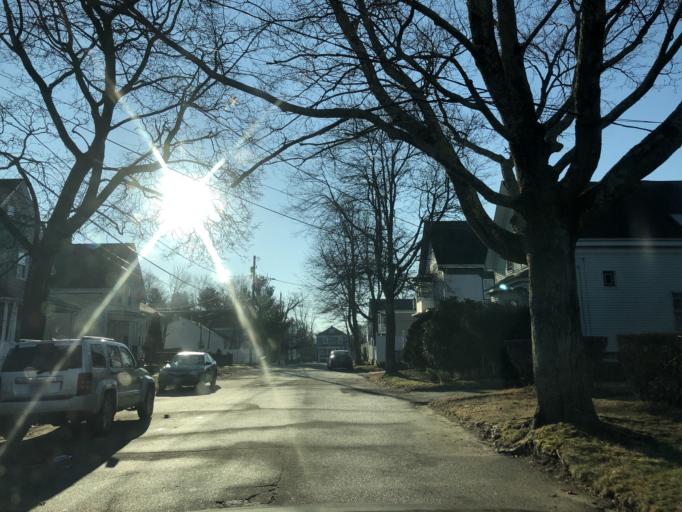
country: US
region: Massachusetts
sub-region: Plymouth County
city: Brockton
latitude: 42.1010
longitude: -71.0238
